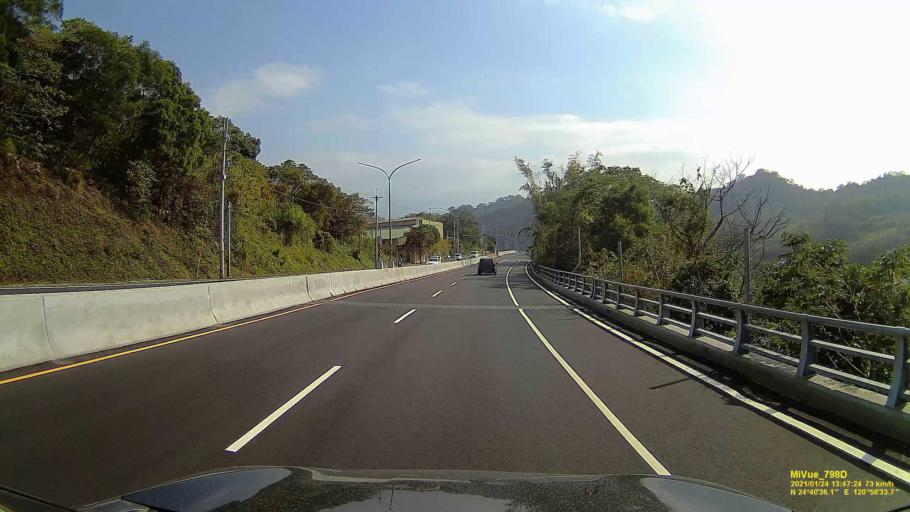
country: TW
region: Taiwan
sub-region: Hsinchu
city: Hsinchu
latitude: 24.6765
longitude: 120.9428
